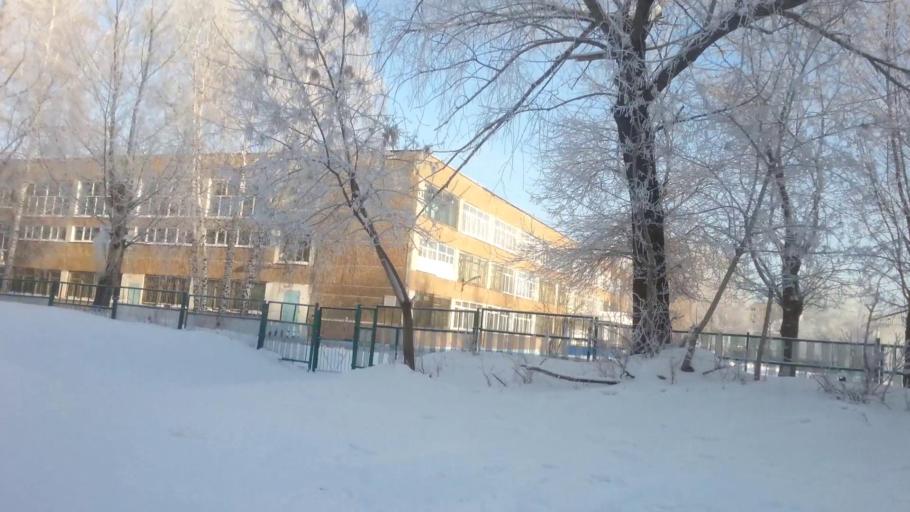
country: RU
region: Altai Krai
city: Novosilikatnyy
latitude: 53.3776
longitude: 83.6731
